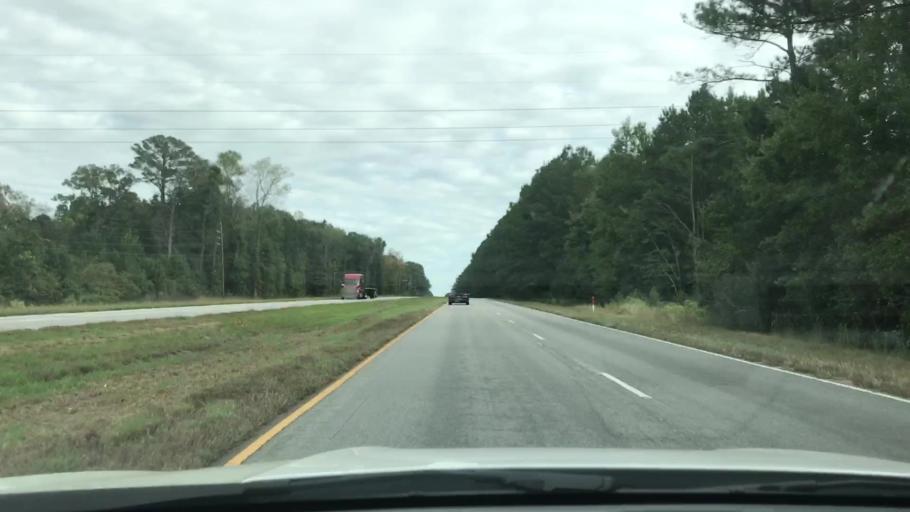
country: US
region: South Carolina
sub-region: Charleston County
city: Ravenel
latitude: 32.7564
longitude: -80.3619
